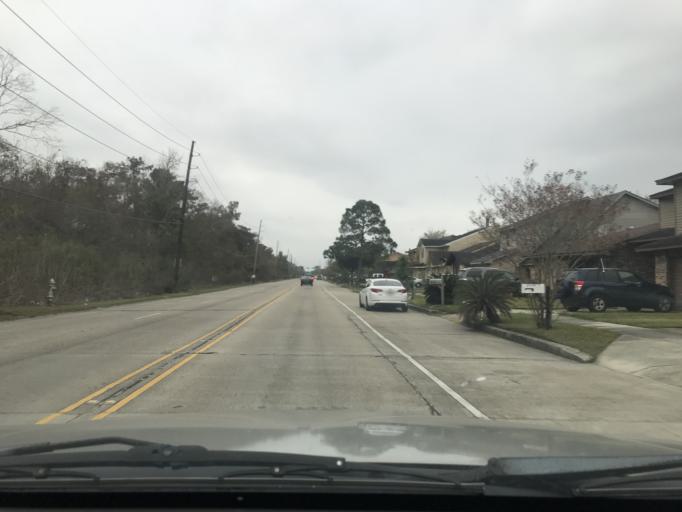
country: US
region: Louisiana
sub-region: Jefferson Parish
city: Woodmere
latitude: 29.8609
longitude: -90.0726
